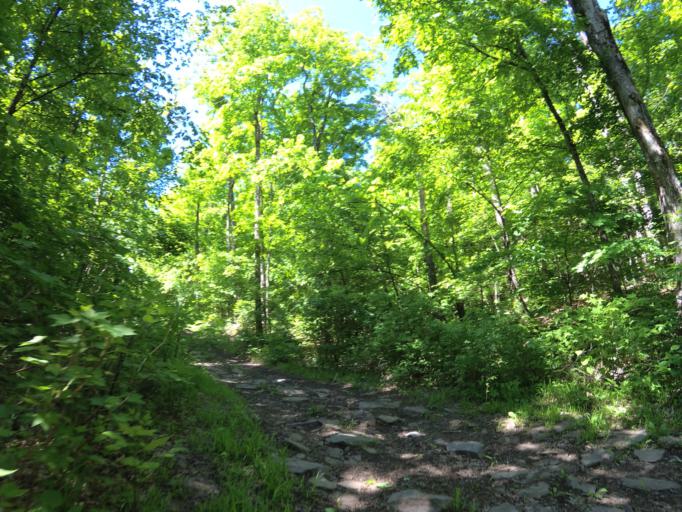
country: CA
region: Ontario
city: Renfrew
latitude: 45.0552
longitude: -77.0853
